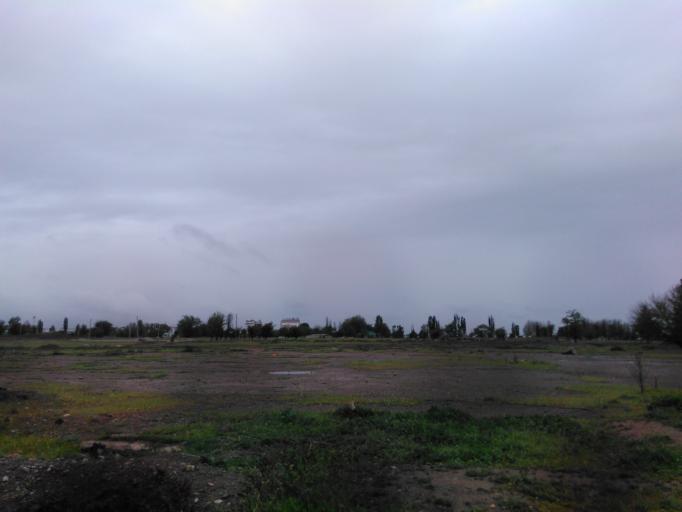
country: KG
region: Chuy
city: Tokmok
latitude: 42.8110
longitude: 75.3306
